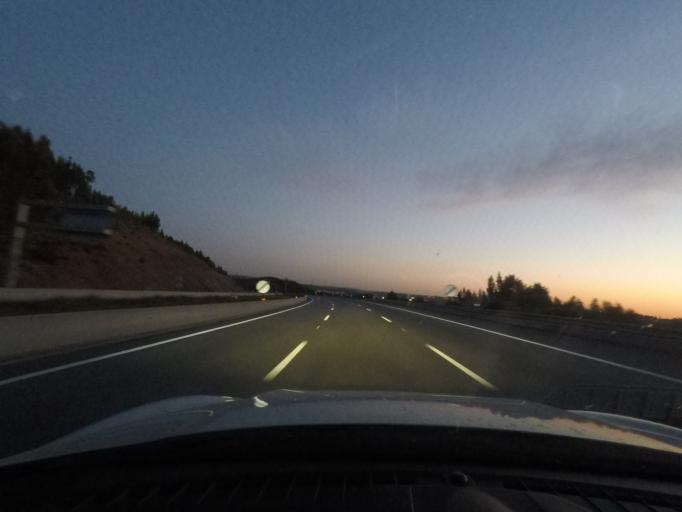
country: PT
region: Porto
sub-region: Gondomar
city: Foz do Sousa
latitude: 41.0989
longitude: -8.4568
